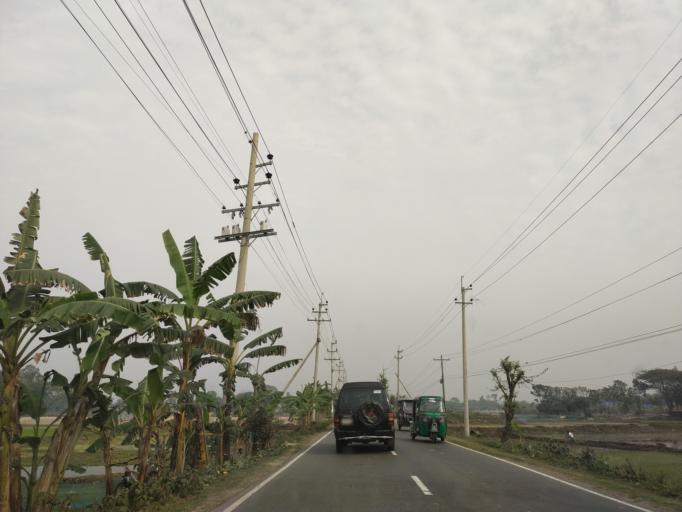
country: BD
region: Dhaka
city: Narsingdi
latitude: 23.9896
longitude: 90.7360
